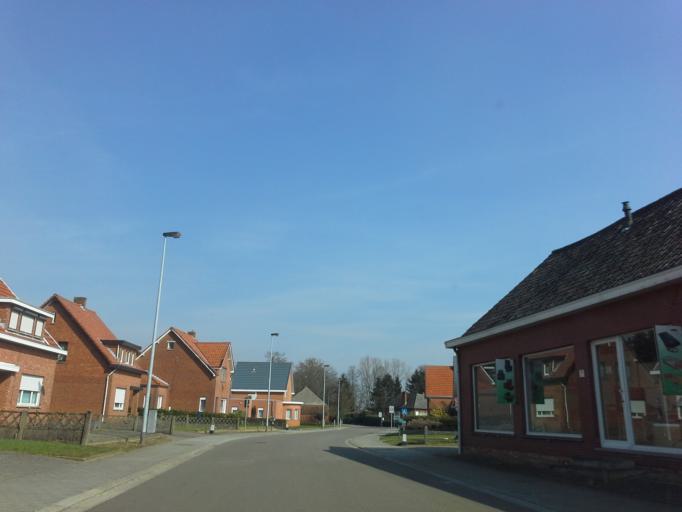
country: BE
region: Flanders
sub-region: Provincie Antwerpen
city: Meerhout
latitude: 51.1355
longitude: 5.0736
